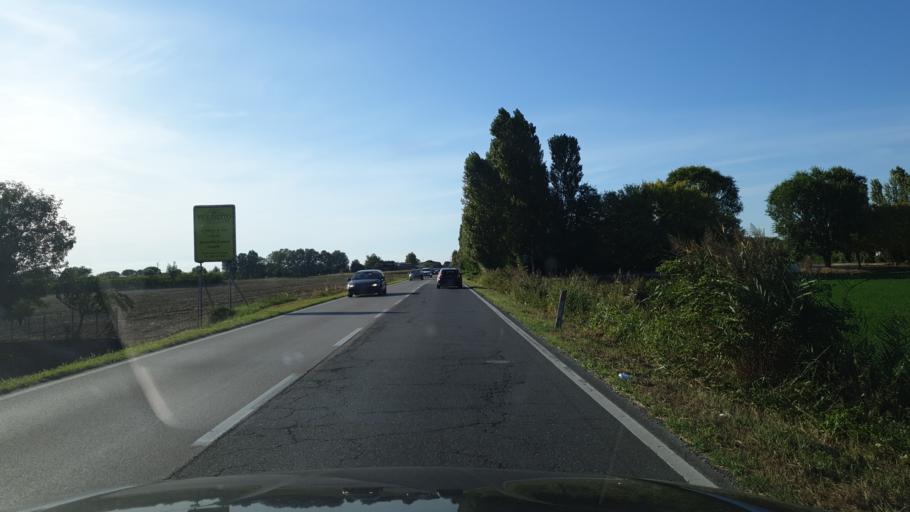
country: IT
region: Emilia-Romagna
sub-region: Provincia di Ravenna
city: Mezzano
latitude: 44.4511
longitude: 12.1167
